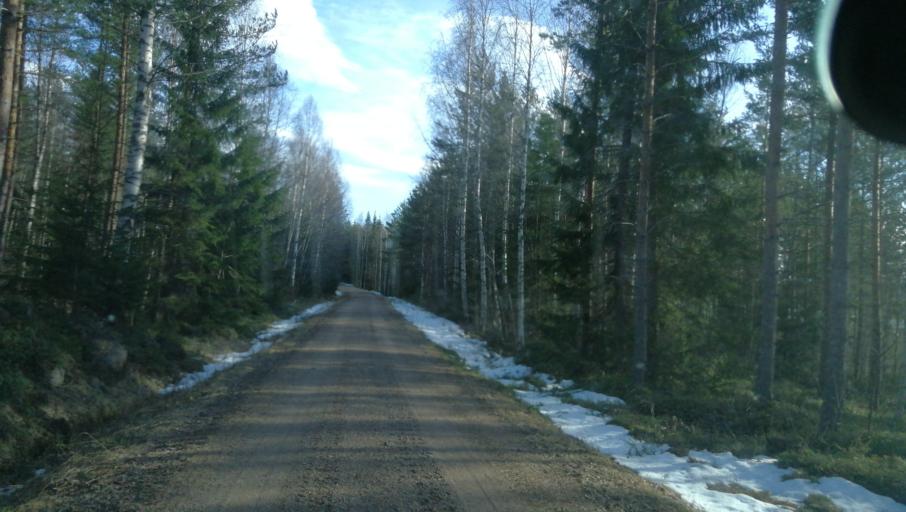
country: SE
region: Dalarna
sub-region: Vansbro Kommun
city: Vansbro
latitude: 60.8049
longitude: 14.2090
